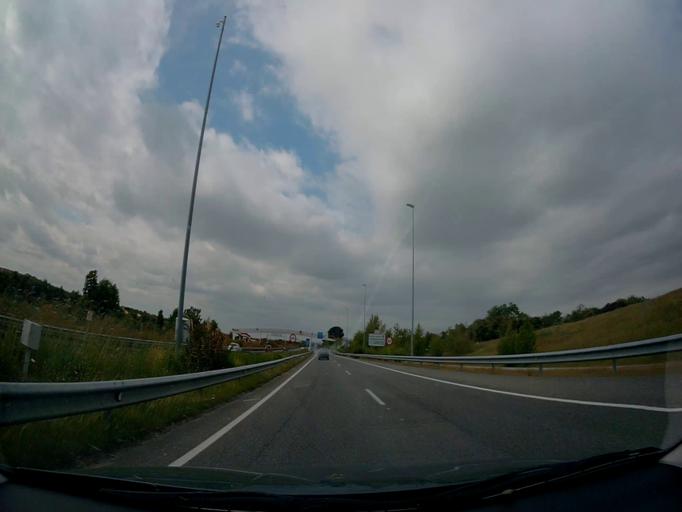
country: ES
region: Madrid
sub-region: Provincia de Madrid
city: Boadilla del Monte
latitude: 40.3926
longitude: -3.8955
